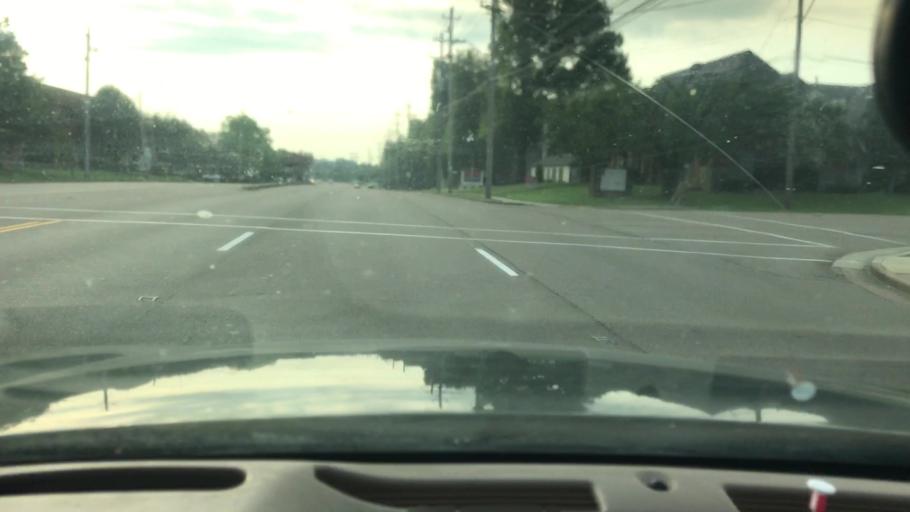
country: US
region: Tennessee
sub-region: Shelby County
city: Bartlett
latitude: 35.2047
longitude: -89.8454
